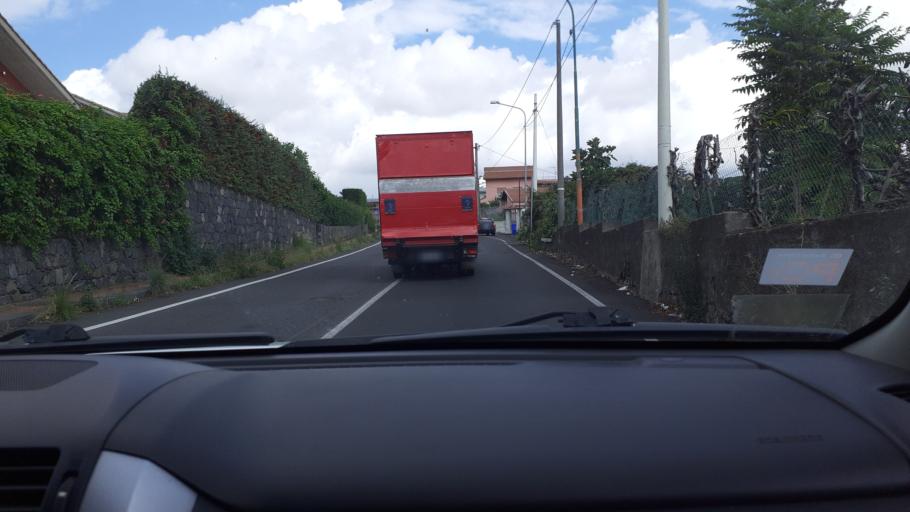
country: IT
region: Sicily
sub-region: Catania
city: Cerza
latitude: 37.5477
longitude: 15.1005
